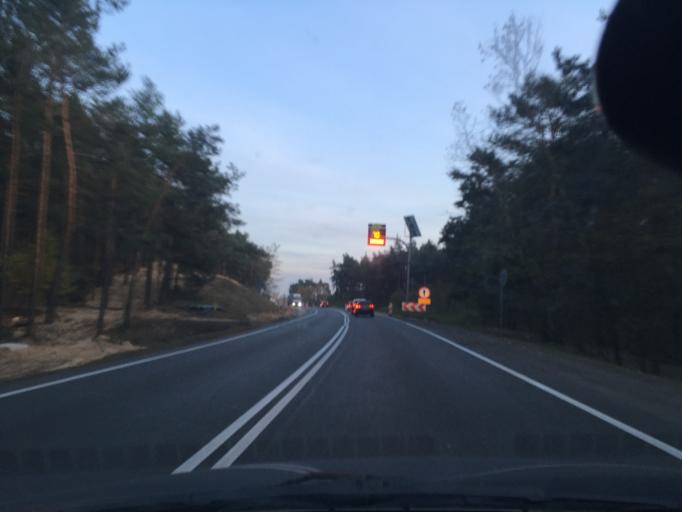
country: PL
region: Masovian Voivodeship
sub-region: Powiat plocki
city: Wyszogrod
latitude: 52.3634
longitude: 20.1955
